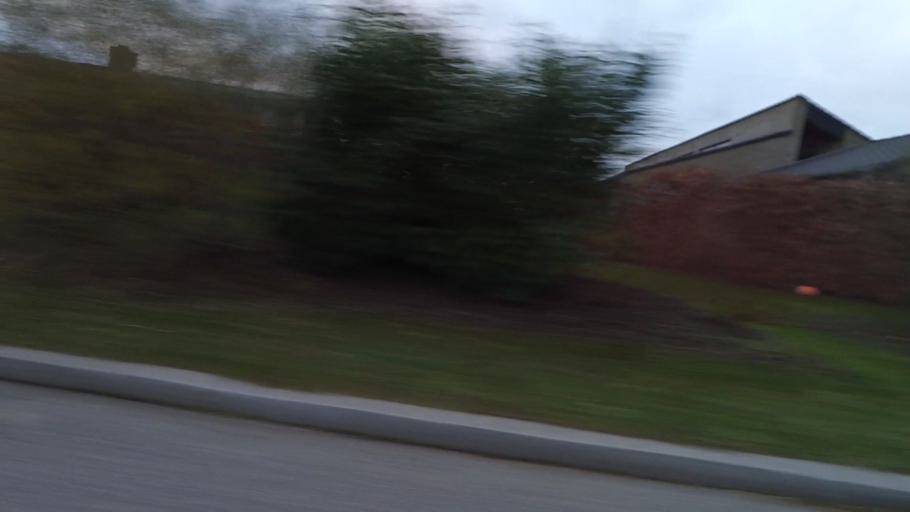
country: DK
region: Central Jutland
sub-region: Arhus Kommune
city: Stavtrup
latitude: 56.1584
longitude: 10.0940
